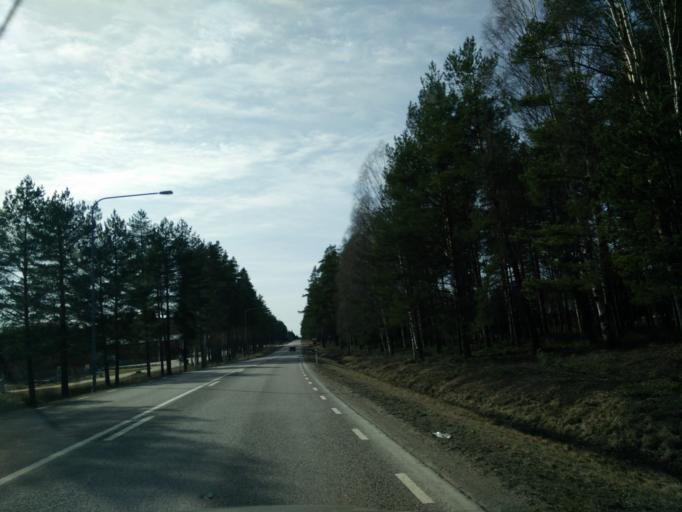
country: SE
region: Vaermland
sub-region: Hagfors Kommun
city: Hagfors
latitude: 60.0128
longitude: 13.6753
